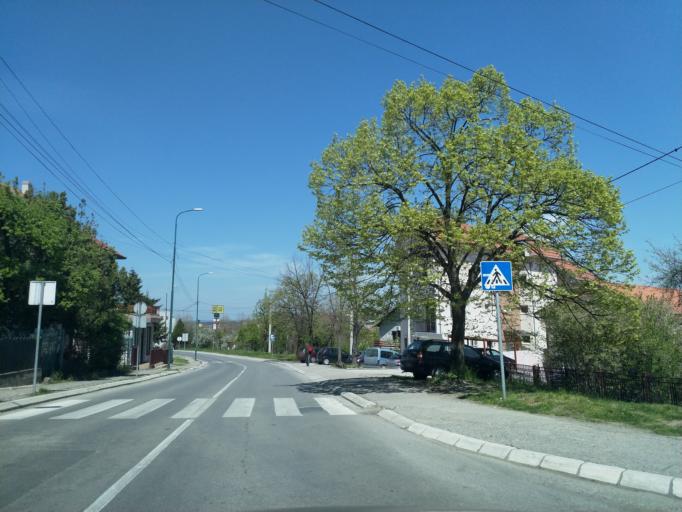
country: RS
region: Central Serbia
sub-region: Belgrade
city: Lazarevac
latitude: 44.3833
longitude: 20.2505
